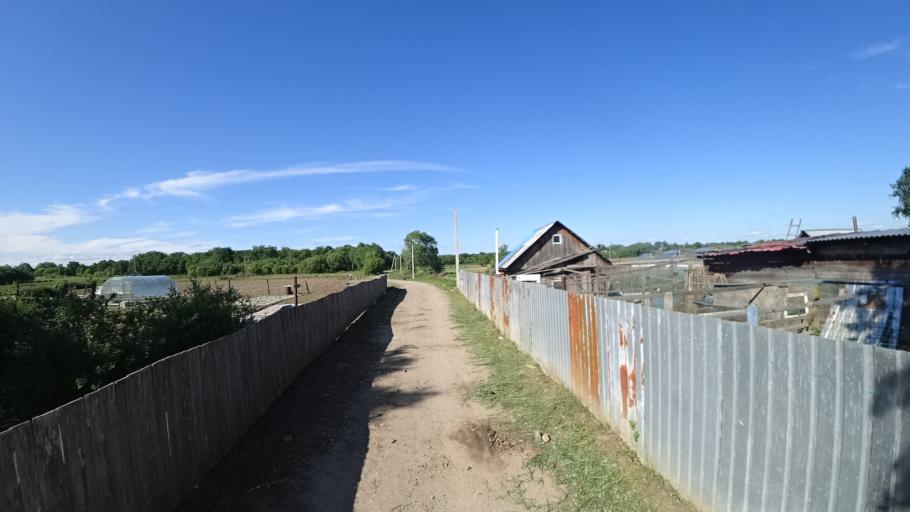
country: RU
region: Khabarovsk Krai
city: Khor
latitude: 47.8854
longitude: 135.0184
